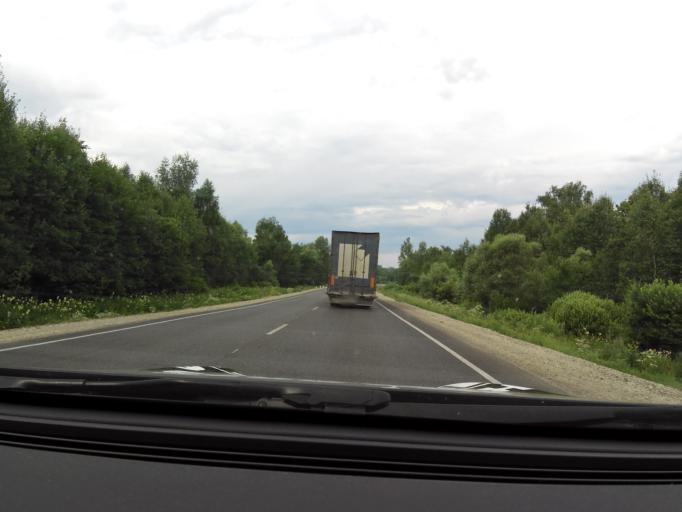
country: RU
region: Bashkortostan
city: Ulu-Telyak
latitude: 54.8480
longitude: 57.1064
